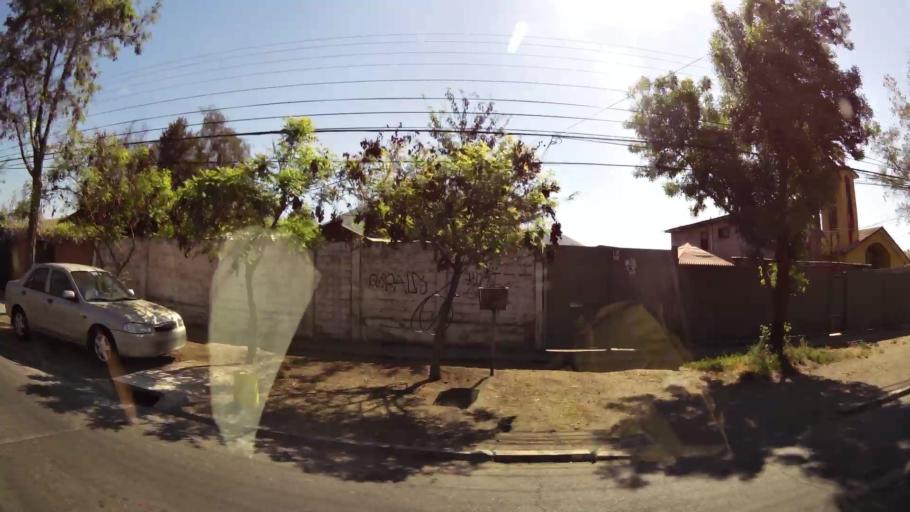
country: CL
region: Santiago Metropolitan
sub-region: Provincia de Maipo
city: San Bernardo
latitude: -33.5988
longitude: -70.7125
